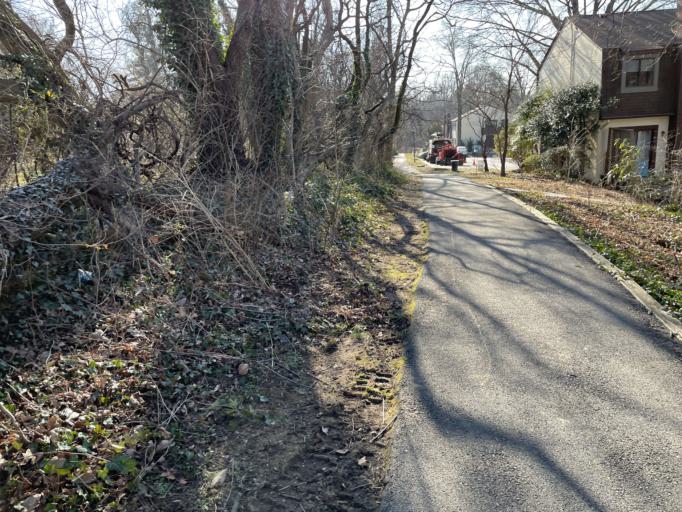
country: US
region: Maryland
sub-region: Howard County
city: Columbia
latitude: 39.2222
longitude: -76.8197
